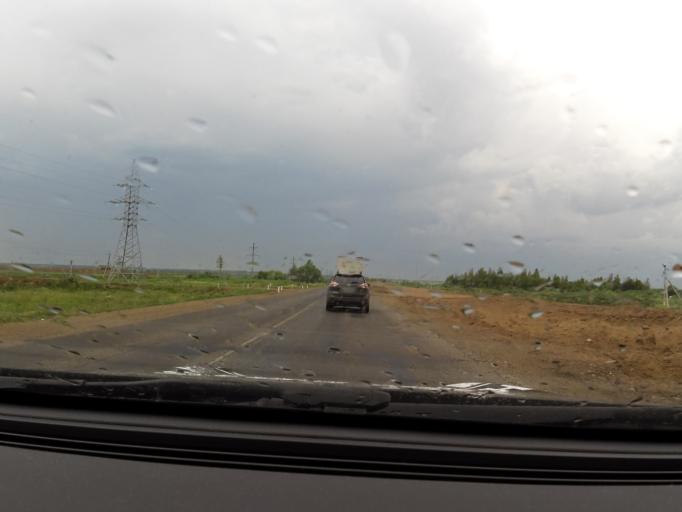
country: RU
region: Bashkortostan
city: Asanovo
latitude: 54.9048
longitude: 55.6185
